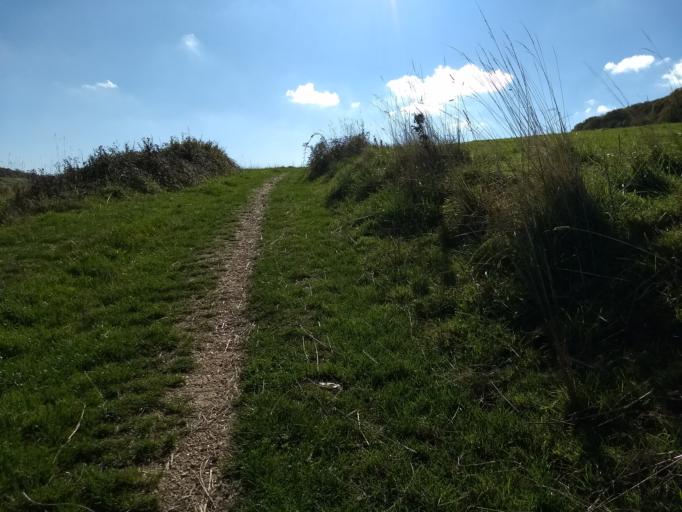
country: GB
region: England
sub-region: Isle of Wight
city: Ventnor
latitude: 50.6147
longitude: -1.2320
